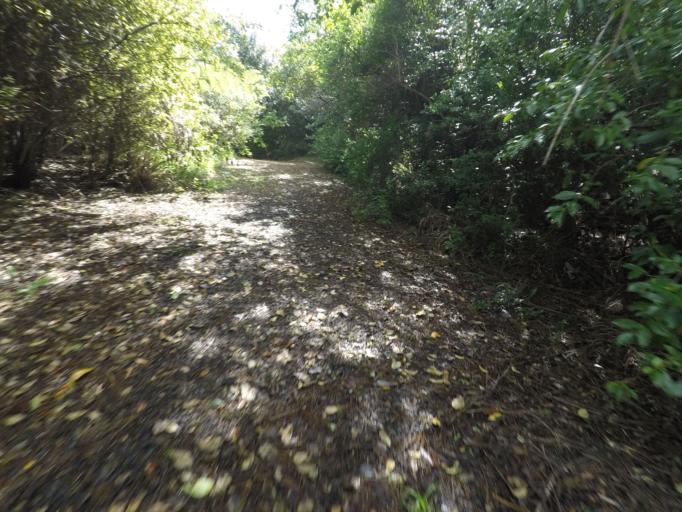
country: NZ
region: Auckland
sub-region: Auckland
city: Rosebank
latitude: -36.8796
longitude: 174.6679
